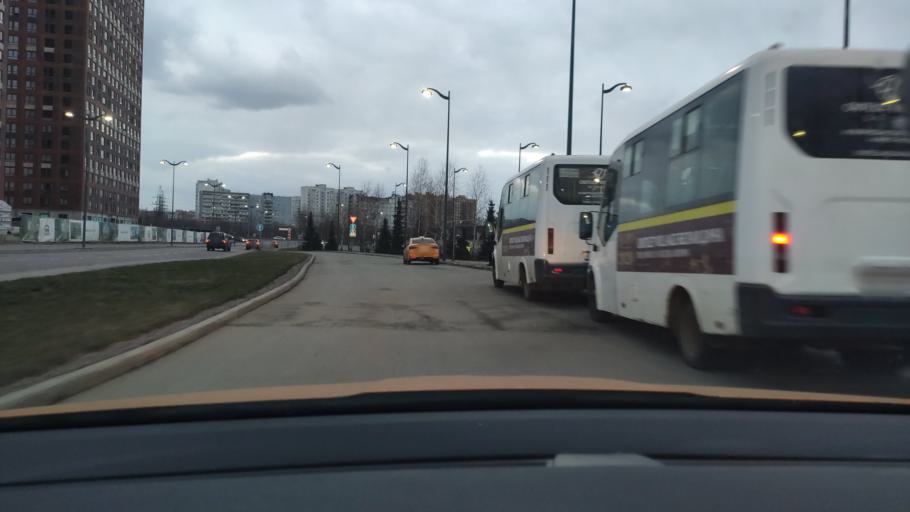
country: RU
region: Moskovskaya
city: Lyubertsy
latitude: 55.6595
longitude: 37.8786
